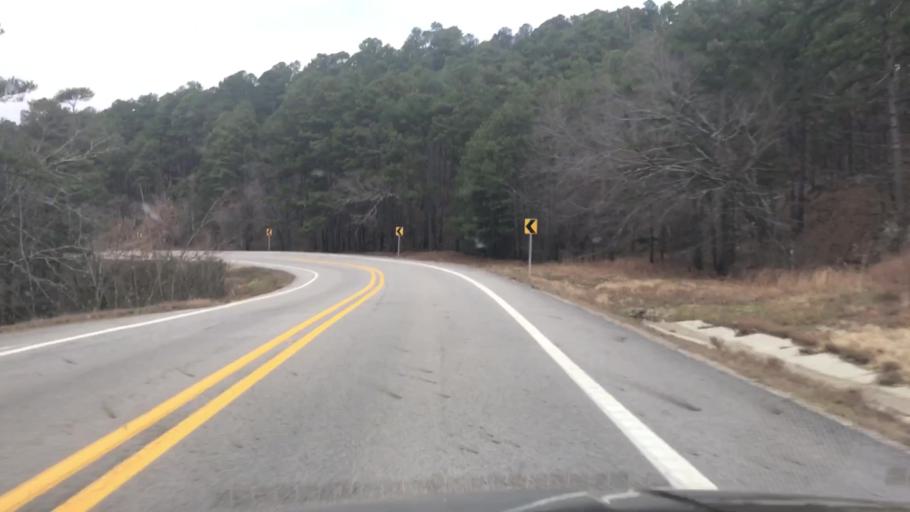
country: US
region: Arkansas
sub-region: Montgomery County
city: Mount Ida
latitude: 34.6829
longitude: -93.7980
